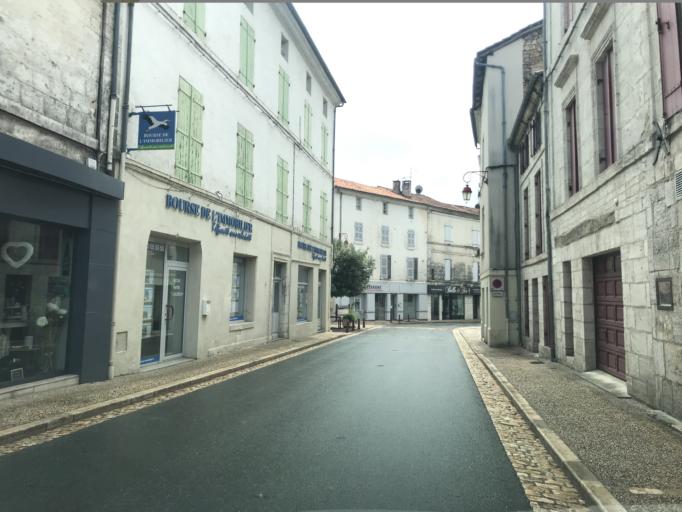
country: FR
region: Aquitaine
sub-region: Departement de la Dordogne
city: Brantome
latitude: 45.3643
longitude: 0.6498
